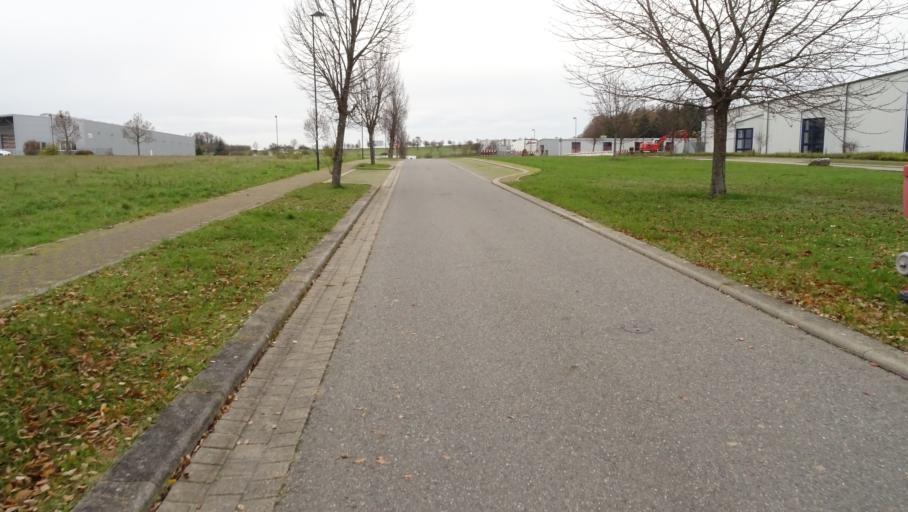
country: DE
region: Baden-Wuerttemberg
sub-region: Karlsruhe Region
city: Binau
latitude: 49.3452
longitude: 9.0444
